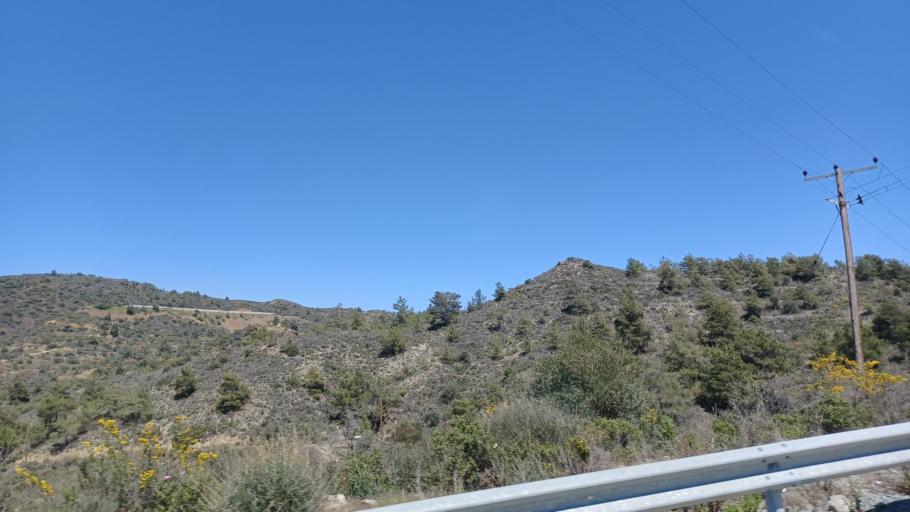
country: CY
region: Limassol
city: Parekklisha
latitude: 34.8135
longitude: 33.1471
